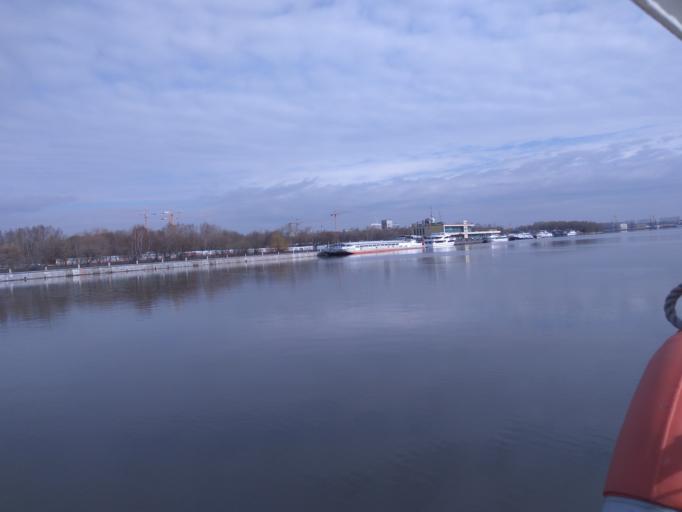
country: RU
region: Moskovskaya
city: Kozhukhovo
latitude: 55.6862
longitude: 37.6714
